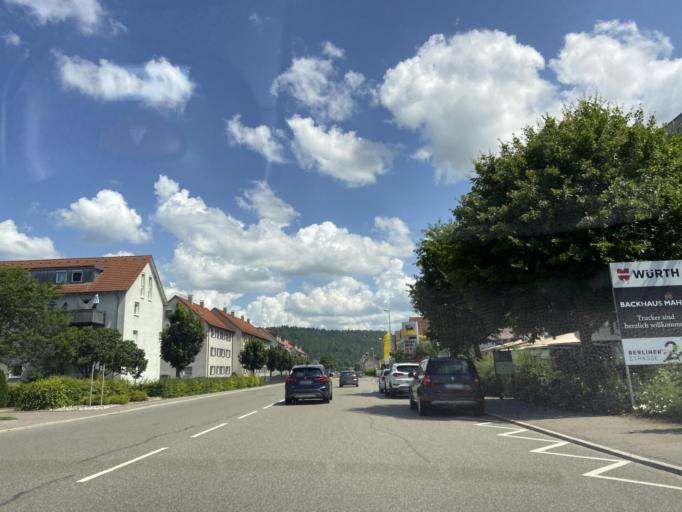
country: DE
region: Baden-Wuerttemberg
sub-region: Tuebingen Region
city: Albstadt
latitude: 48.2066
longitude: 9.0334
